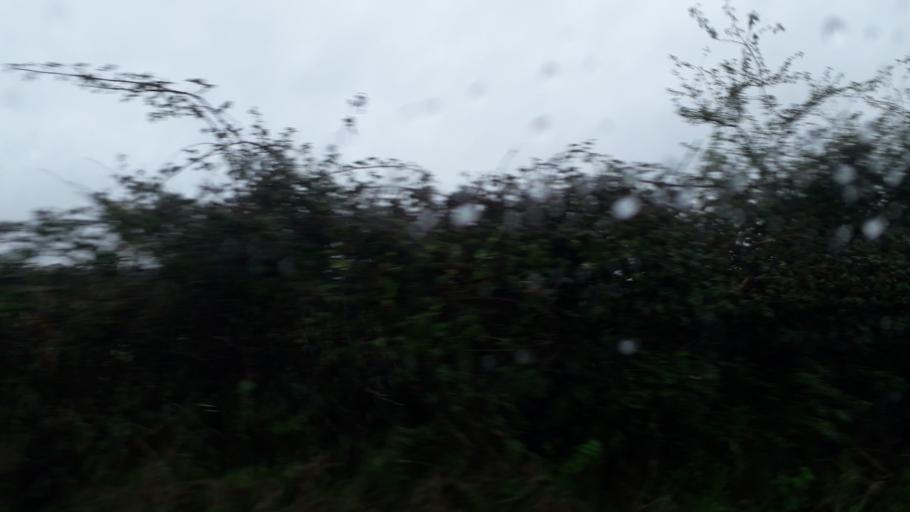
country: IE
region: Connaught
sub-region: Roscommon
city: Roscommon
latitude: 53.7854
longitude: -8.2654
